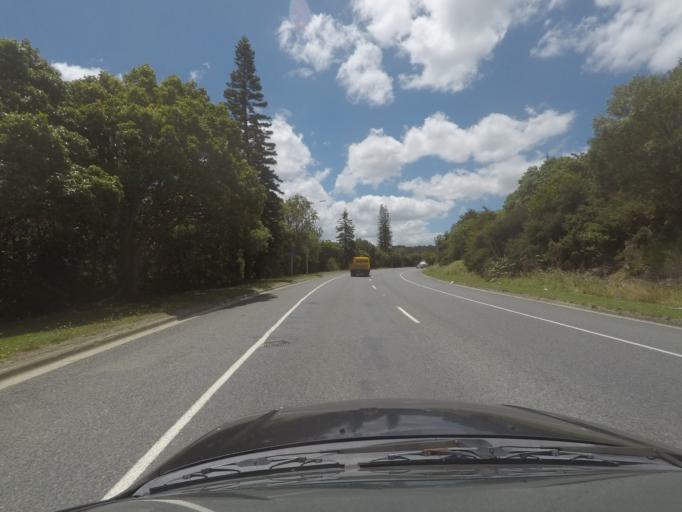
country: NZ
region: Northland
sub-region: Whangarei
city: Whangarei
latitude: -35.7474
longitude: 174.3209
